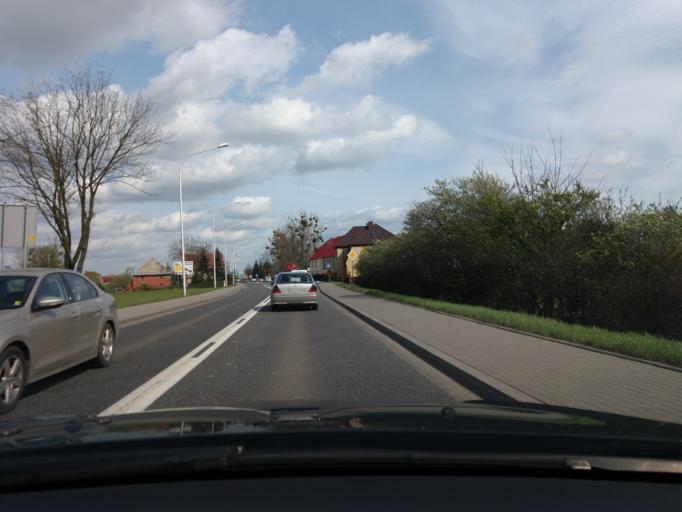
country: PL
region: Lower Silesian Voivodeship
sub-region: Powiat sredzki
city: Mrozow
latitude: 51.1582
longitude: 16.7817
